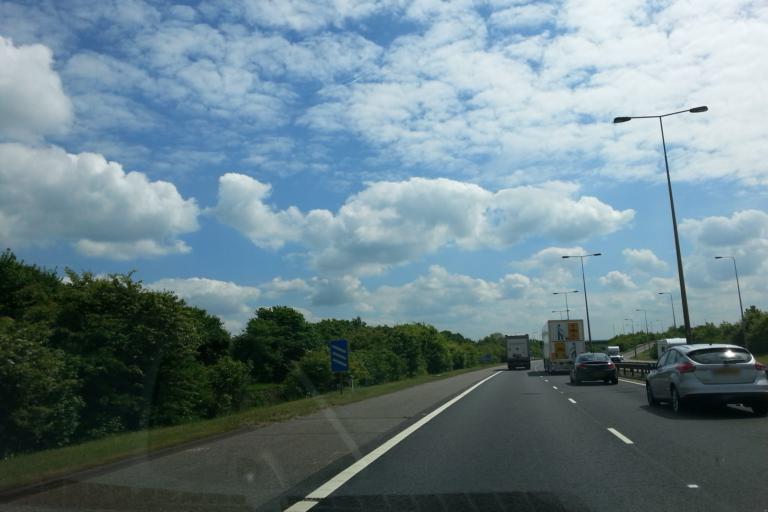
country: GB
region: England
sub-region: Cambridgeshire
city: Great Stukeley
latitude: 52.3757
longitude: -0.2490
